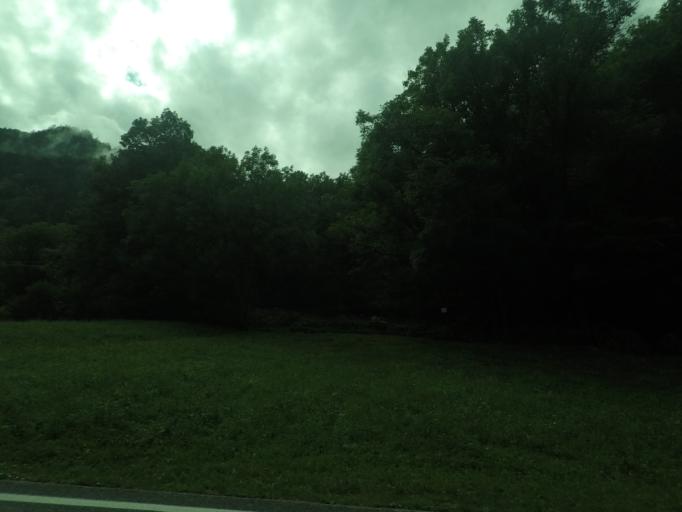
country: IT
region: Aosta Valley
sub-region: Valle d'Aosta
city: Antey-Saint-Andre
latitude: 45.8225
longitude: 7.5894
